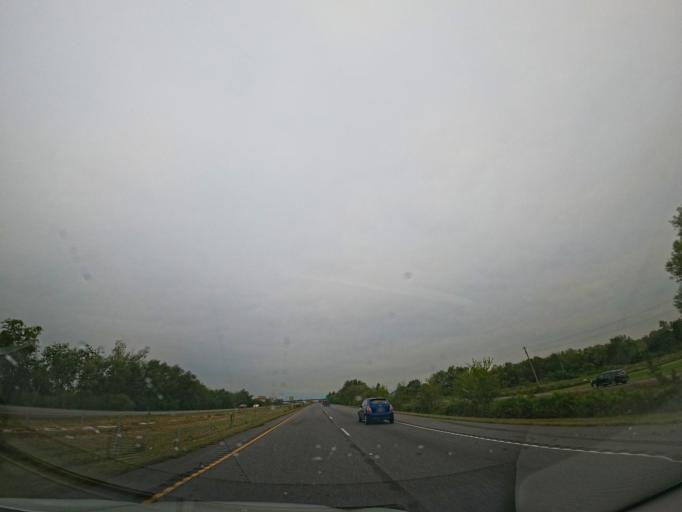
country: US
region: Louisiana
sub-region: Lafourche Parish
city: Raceland
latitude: 29.6905
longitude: -90.5960
